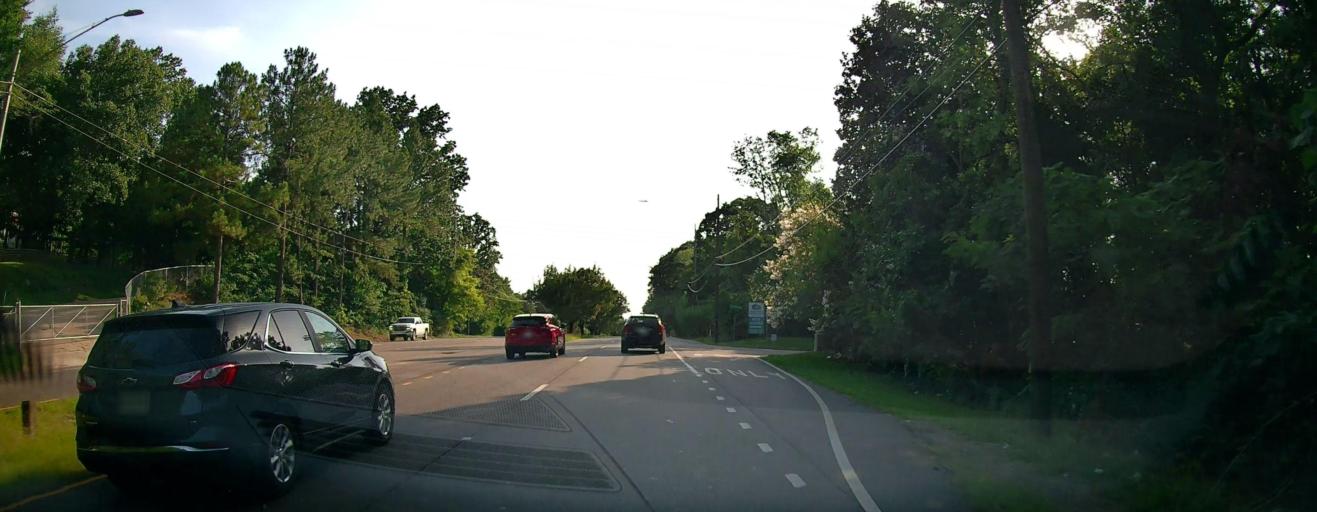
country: US
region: Alabama
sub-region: Jefferson County
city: Irondale
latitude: 33.5315
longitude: -86.7386
